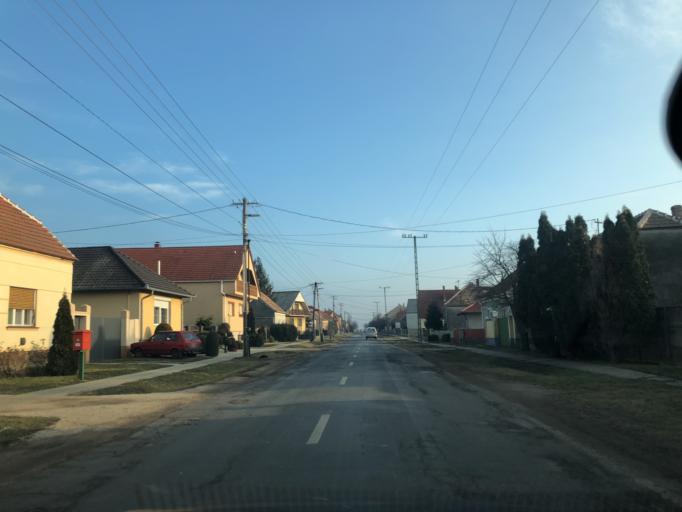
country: HU
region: Gyor-Moson-Sopron
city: Kapuvar
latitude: 47.5937
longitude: 17.0924
